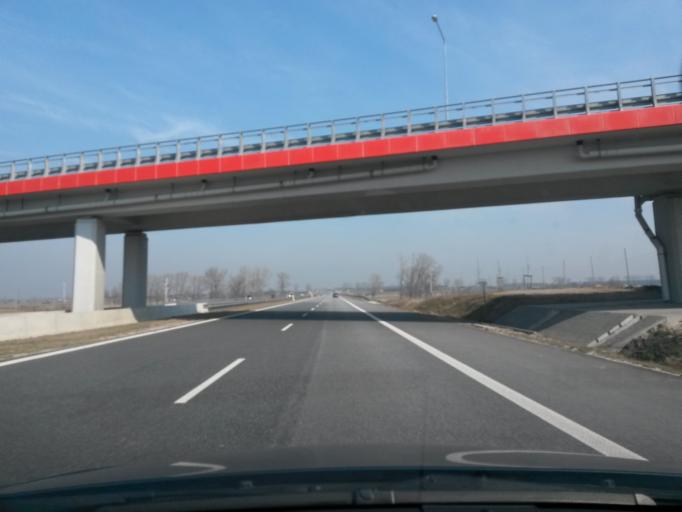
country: PL
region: Lodz Voivodeship
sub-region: Powiat kutnowski
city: Krzyzanow
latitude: 52.1686
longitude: 19.4848
